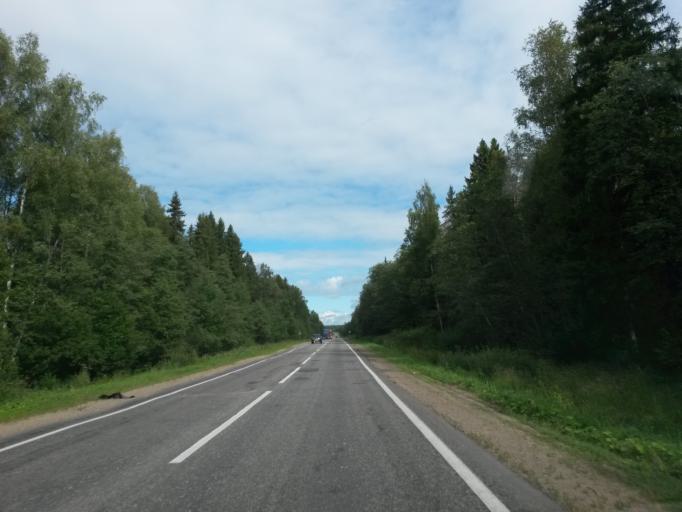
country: RU
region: Jaroslavl
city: Gavrilov-Yam
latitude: 57.4269
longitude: 39.9188
